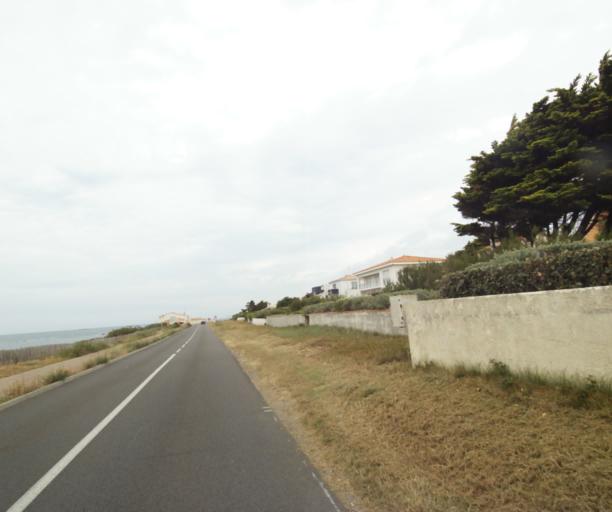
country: FR
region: Pays de la Loire
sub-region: Departement de la Vendee
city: Chateau-d'Olonne
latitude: 46.4661
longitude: -1.7325
